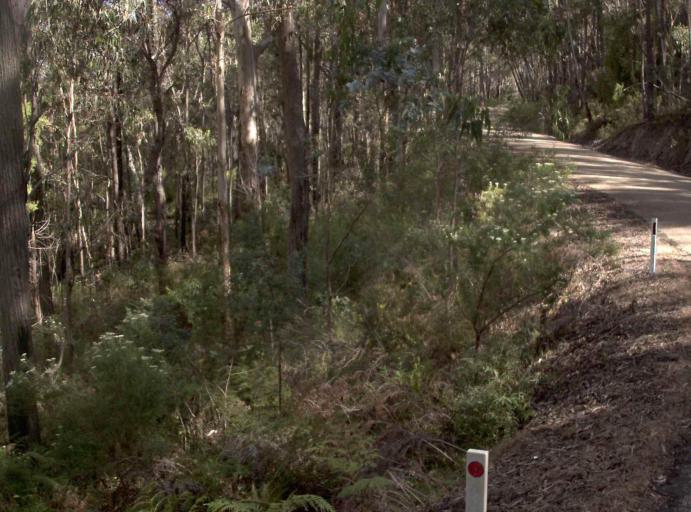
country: AU
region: Victoria
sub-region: East Gippsland
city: Lakes Entrance
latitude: -37.4104
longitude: 148.1229
